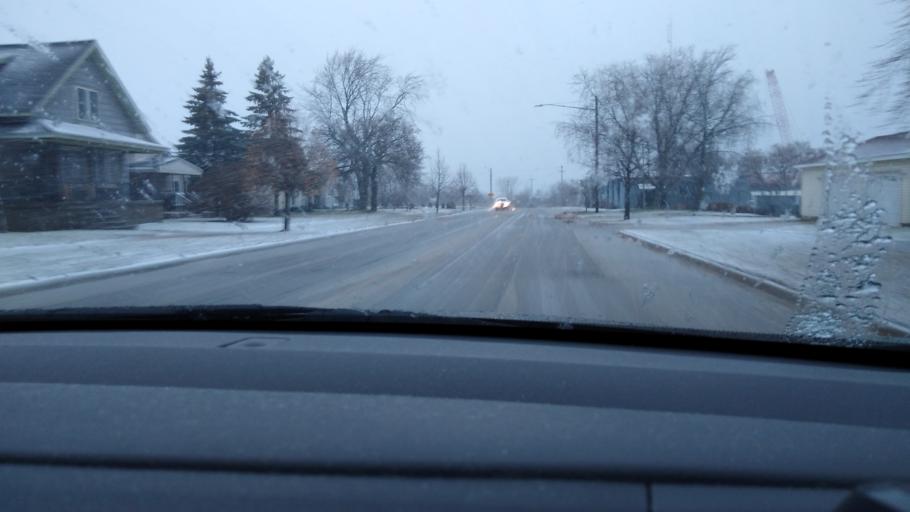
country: US
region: Michigan
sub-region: Delta County
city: Escanaba
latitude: 45.7481
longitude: -87.0612
